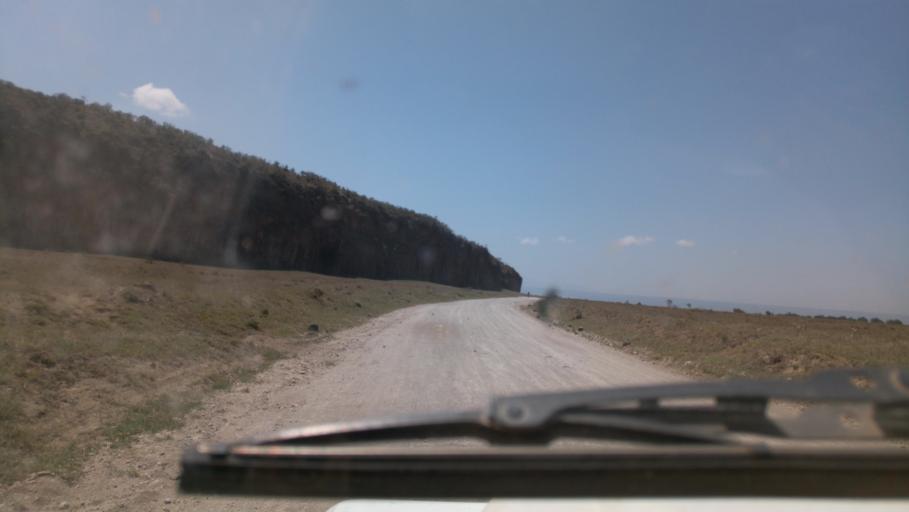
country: KE
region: Nakuru
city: Naivasha
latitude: -0.8590
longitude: 36.3624
